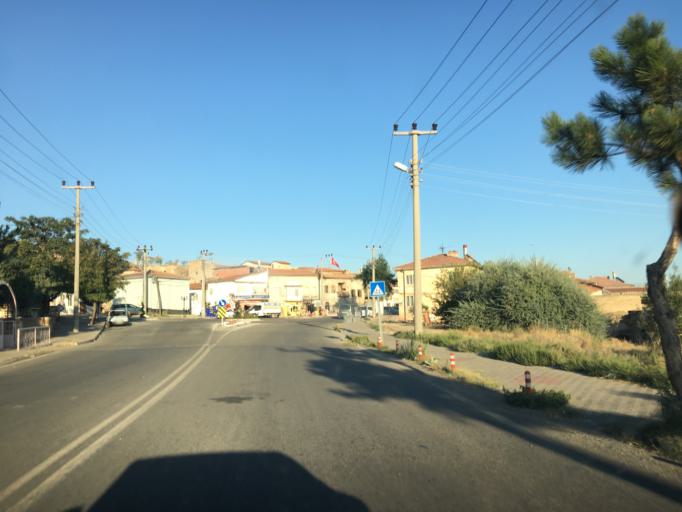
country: TR
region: Nevsehir
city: Avanos
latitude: 38.7188
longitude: 34.8397
